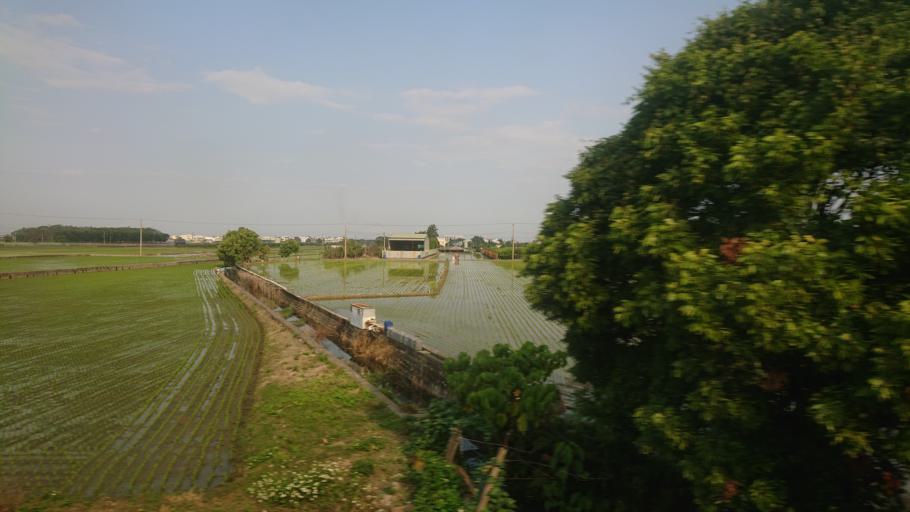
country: TW
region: Taiwan
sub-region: Yunlin
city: Douliu
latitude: 23.6952
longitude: 120.5154
